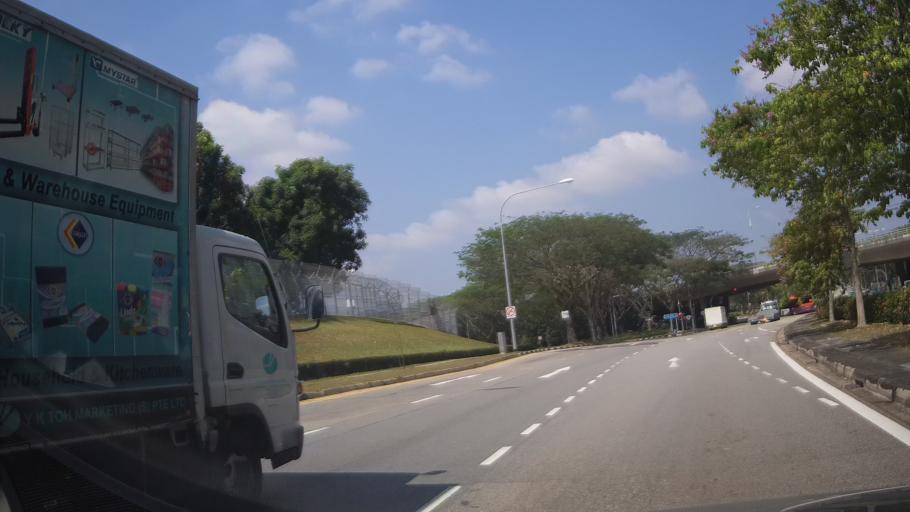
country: SG
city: Singapore
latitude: 1.3634
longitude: 103.9066
